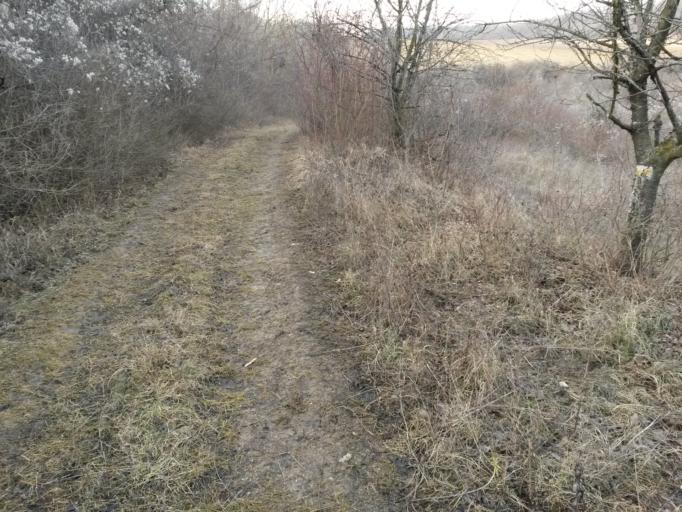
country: HU
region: Pest
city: Perbal
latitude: 47.5951
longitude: 18.7345
